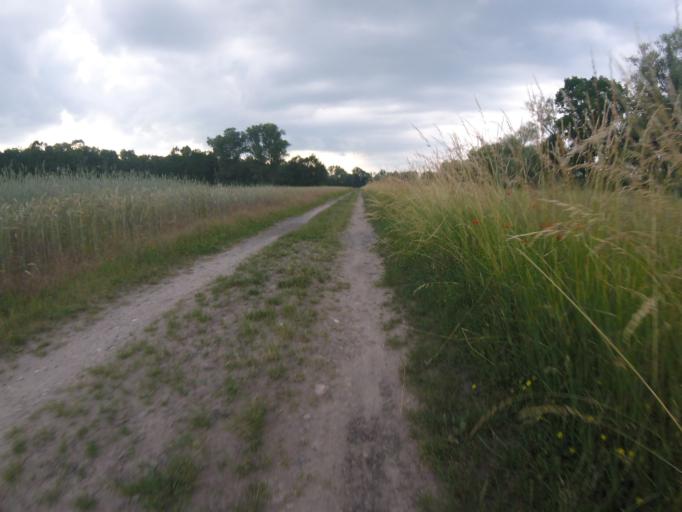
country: DE
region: Brandenburg
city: Konigs Wusterhausen
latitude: 52.2819
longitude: 13.5857
